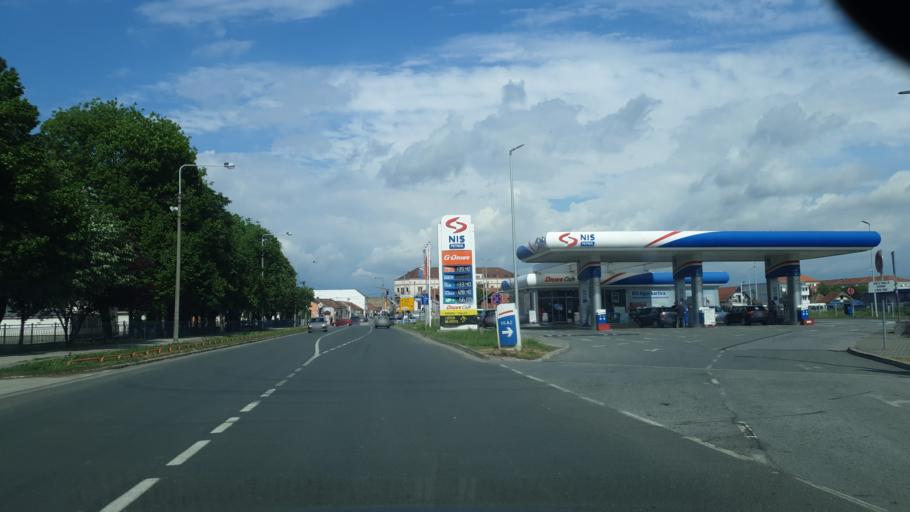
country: RS
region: Central Serbia
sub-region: Belgrade
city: Obrenovac
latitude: 44.6502
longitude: 20.1926
